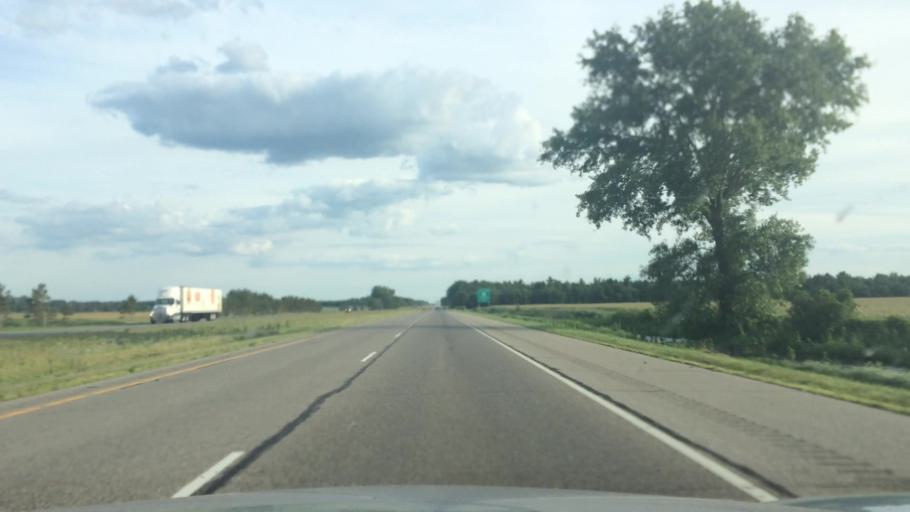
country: US
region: Wisconsin
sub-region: Portage County
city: Plover
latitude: 44.2801
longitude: -89.5237
